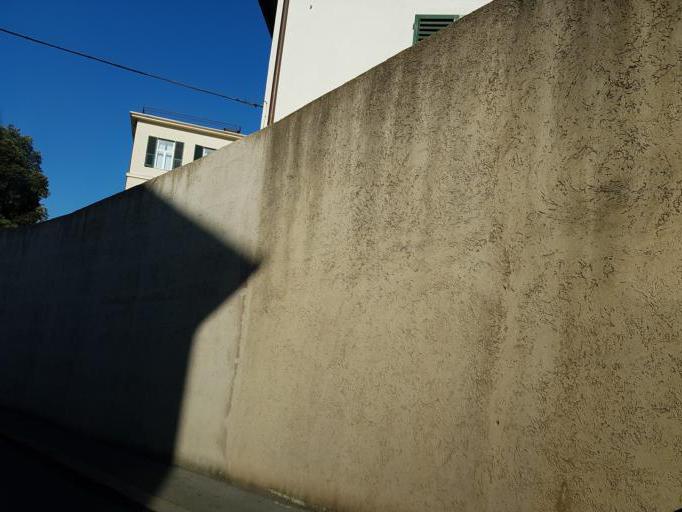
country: IT
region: Liguria
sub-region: Provincia di Genova
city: San Teodoro
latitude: 44.4175
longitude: 8.8749
